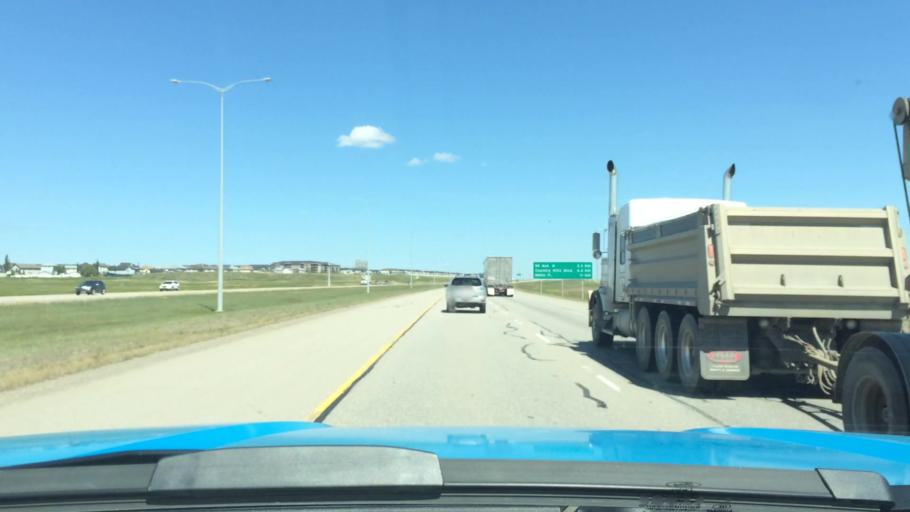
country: CA
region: Alberta
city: Chestermere
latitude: 51.1097
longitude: -113.9198
